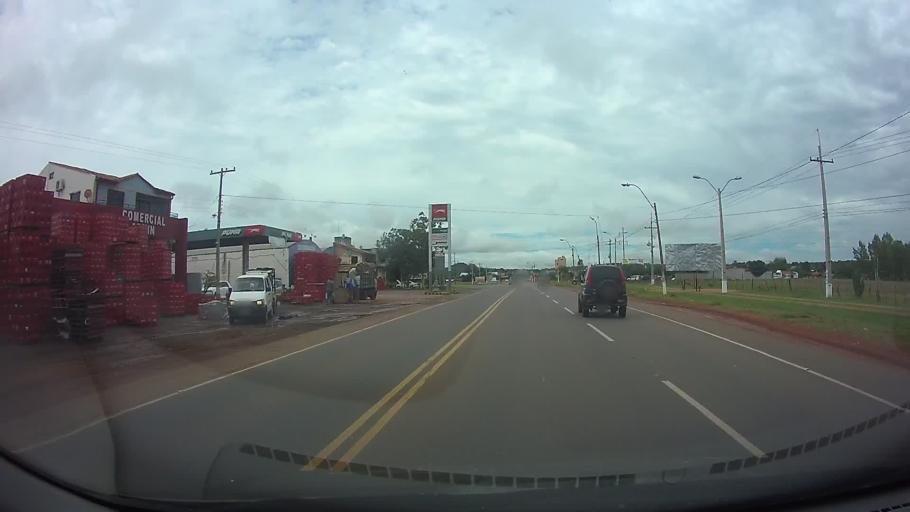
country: PY
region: Paraguari
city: Carapegua
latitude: -25.7607
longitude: -57.2320
